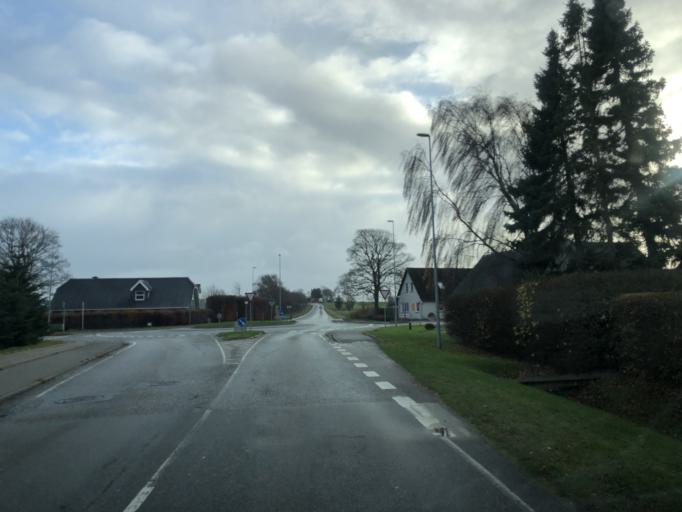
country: DK
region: North Denmark
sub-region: Rebild Kommune
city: Stovring
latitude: 56.8872
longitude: 9.7858
